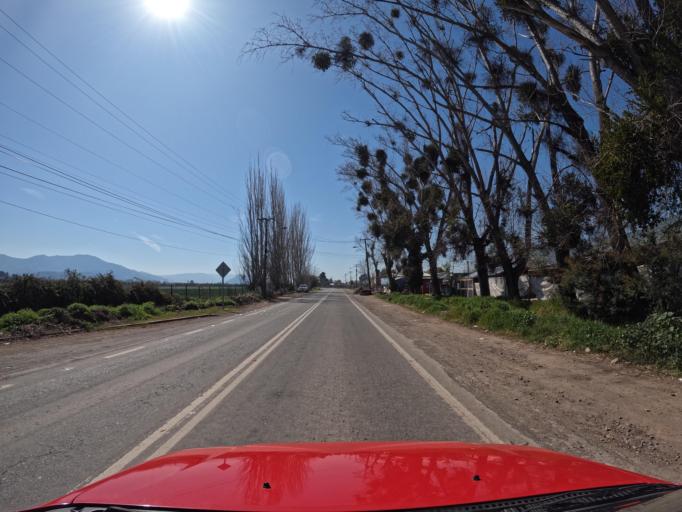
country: CL
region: Maule
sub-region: Provincia de Curico
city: Rauco
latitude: -35.0218
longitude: -71.4302
